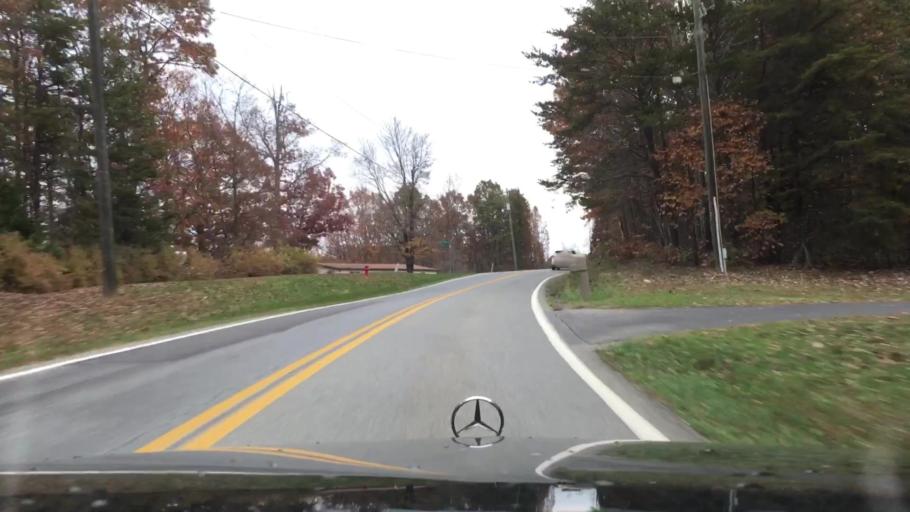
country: US
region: Virginia
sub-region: Campbell County
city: Timberlake
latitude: 37.2601
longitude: -79.2724
